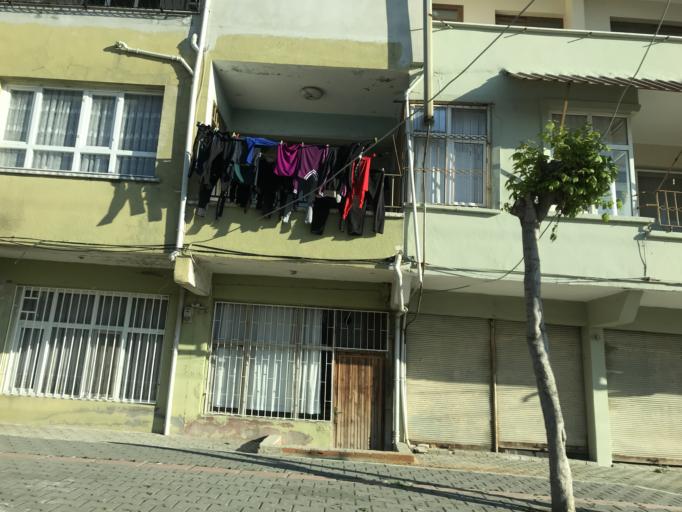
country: TR
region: Hatay
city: Samandag
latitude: 36.0839
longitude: 35.9633
